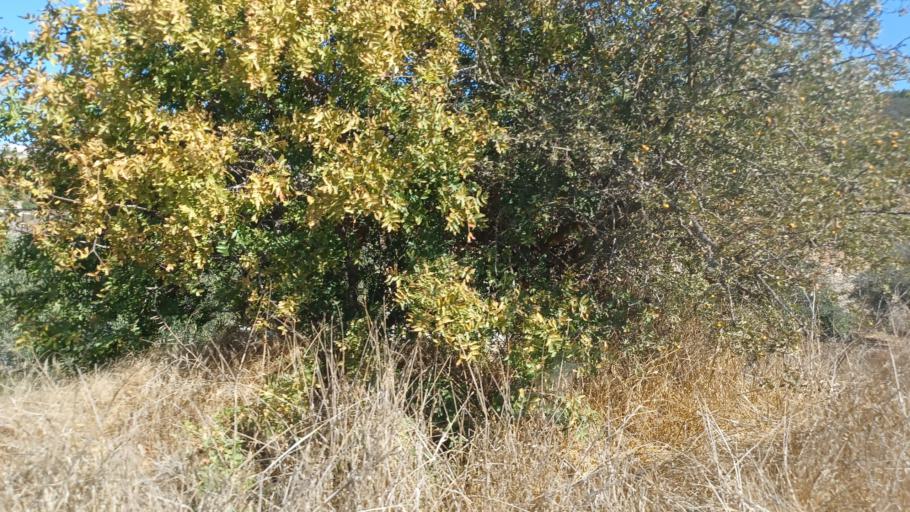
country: CY
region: Pafos
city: Mesogi
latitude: 34.8056
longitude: 32.4849
